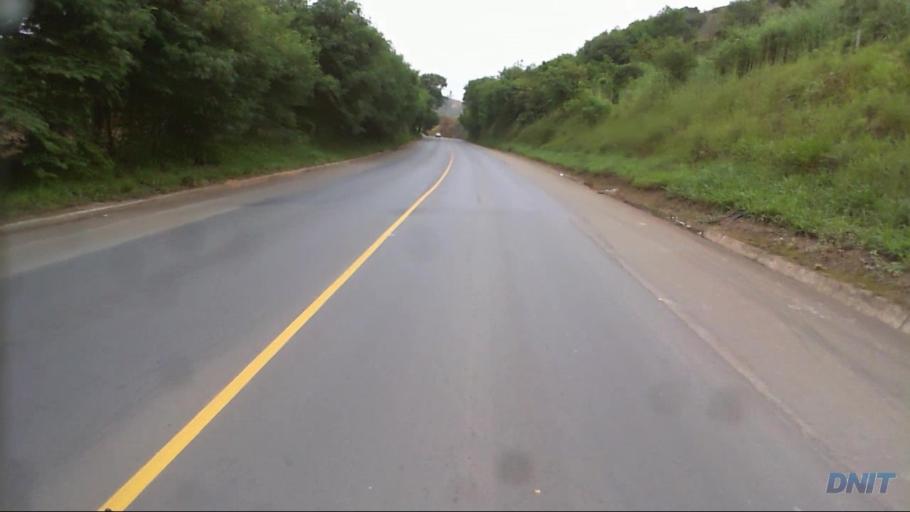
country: BR
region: Minas Gerais
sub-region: Coronel Fabriciano
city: Coronel Fabriciano
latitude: -19.5245
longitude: -42.6593
